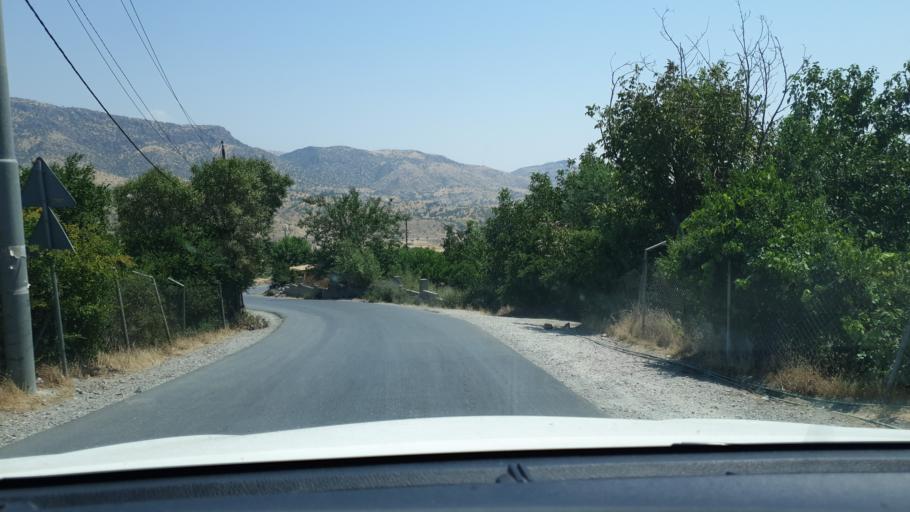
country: IQ
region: Arbil
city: Nahiyat Hiran
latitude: 36.2821
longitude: 44.4931
